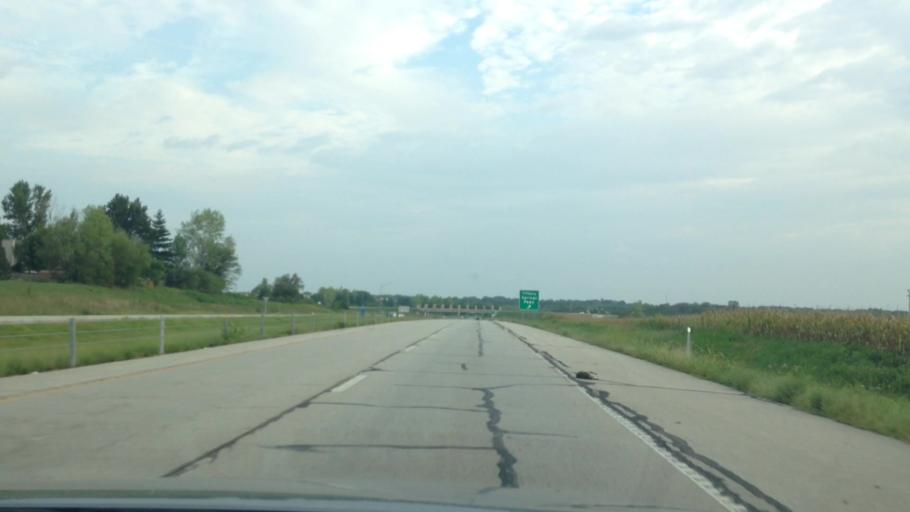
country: US
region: Missouri
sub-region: Clay County
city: Gladstone
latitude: 39.2768
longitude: -94.5851
